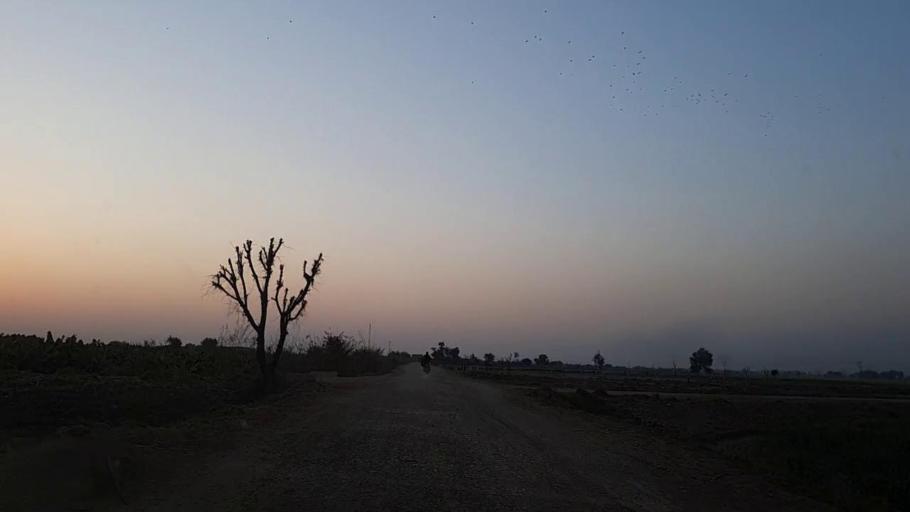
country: PK
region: Sindh
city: Hala
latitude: 25.9446
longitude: 68.4341
